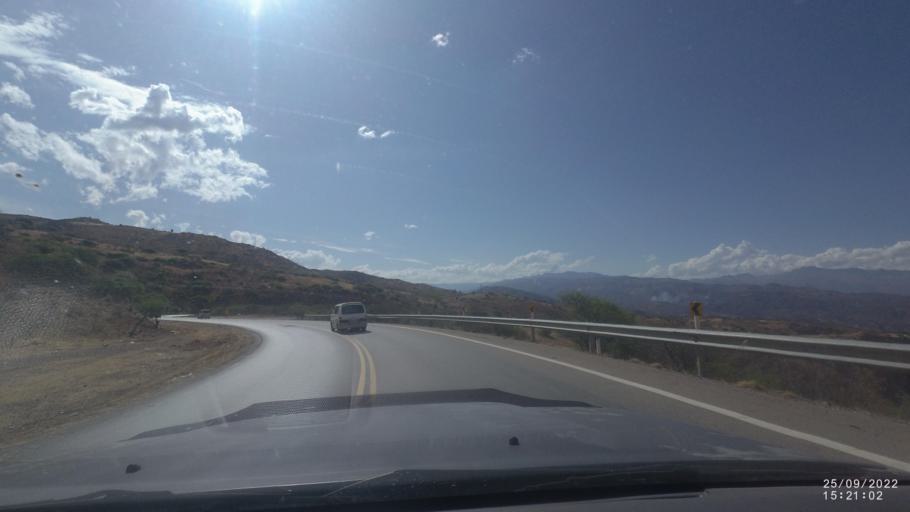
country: BO
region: Cochabamba
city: Irpa Irpa
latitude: -17.6220
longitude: -66.3572
